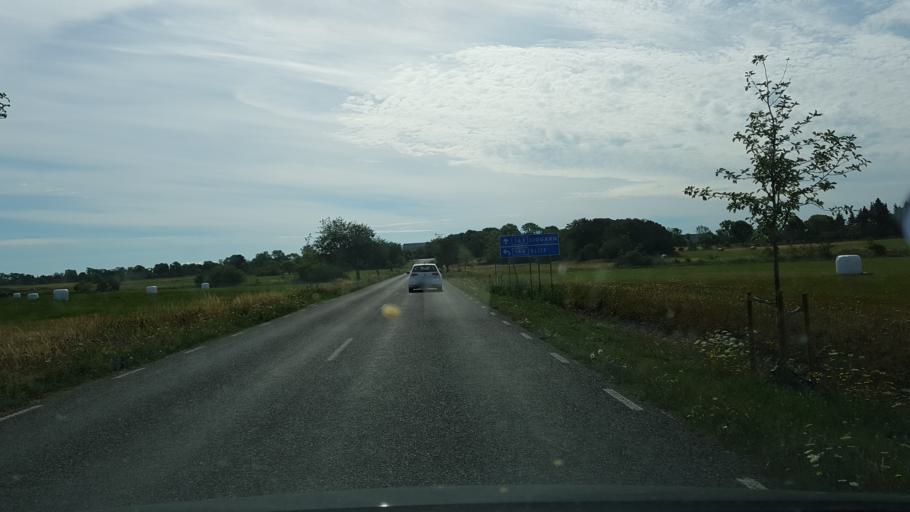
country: SE
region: Gotland
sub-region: Gotland
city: Hemse
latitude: 57.4308
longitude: 18.6237
